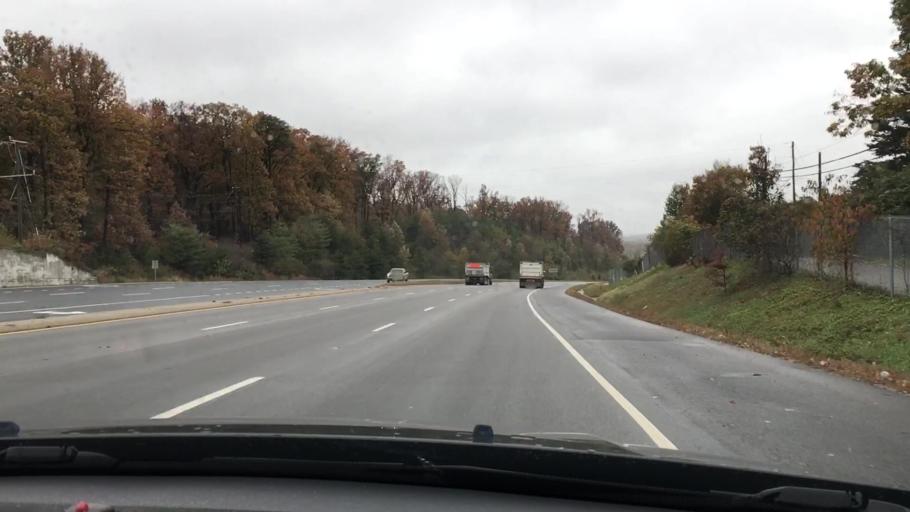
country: US
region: Virginia
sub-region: Fairfax County
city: Lorton
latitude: 38.6930
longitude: -77.2563
